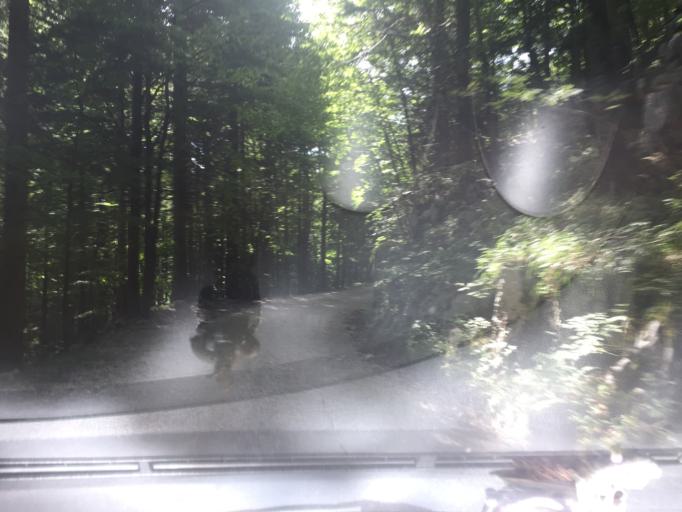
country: SI
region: Ajdovscina
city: Lokavec
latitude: 45.9868
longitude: 13.8383
